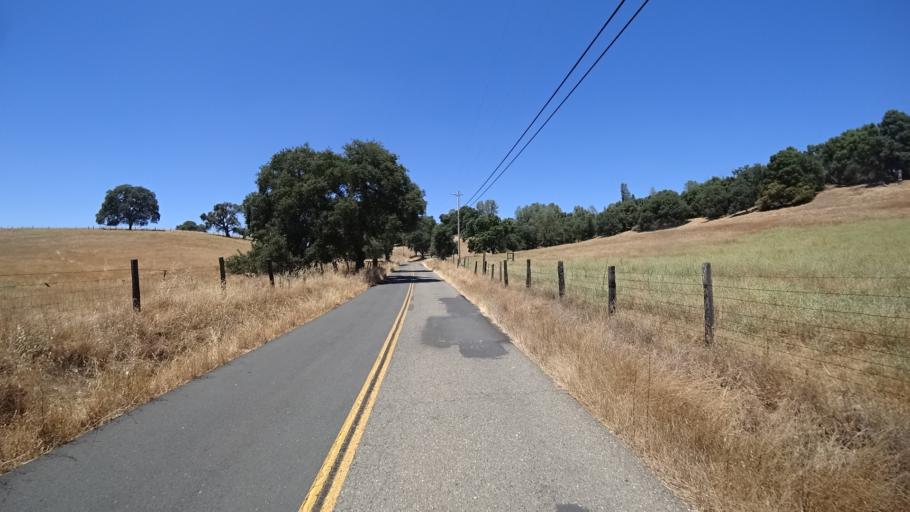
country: US
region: California
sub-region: Calaveras County
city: Mountain Ranch
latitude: 38.2298
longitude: -120.5451
